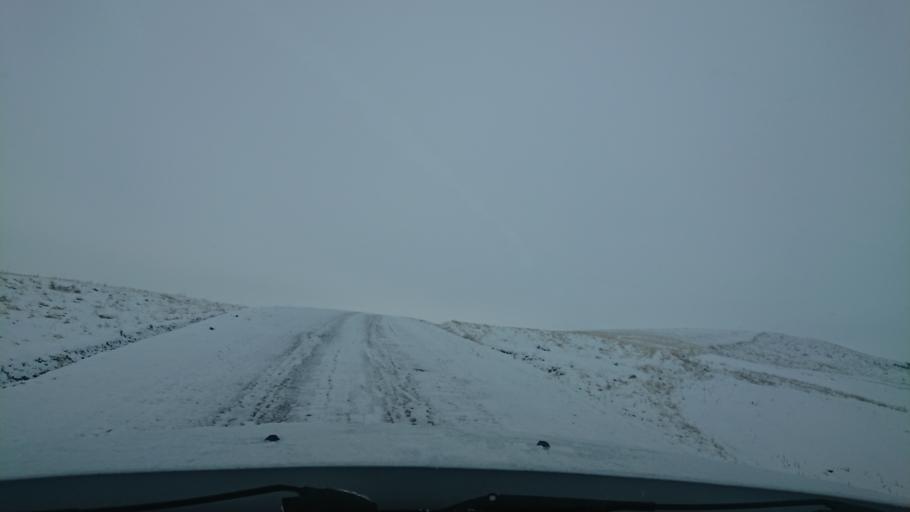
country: TR
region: Aksaray
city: Acipinar
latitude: 38.6883
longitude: 33.8697
